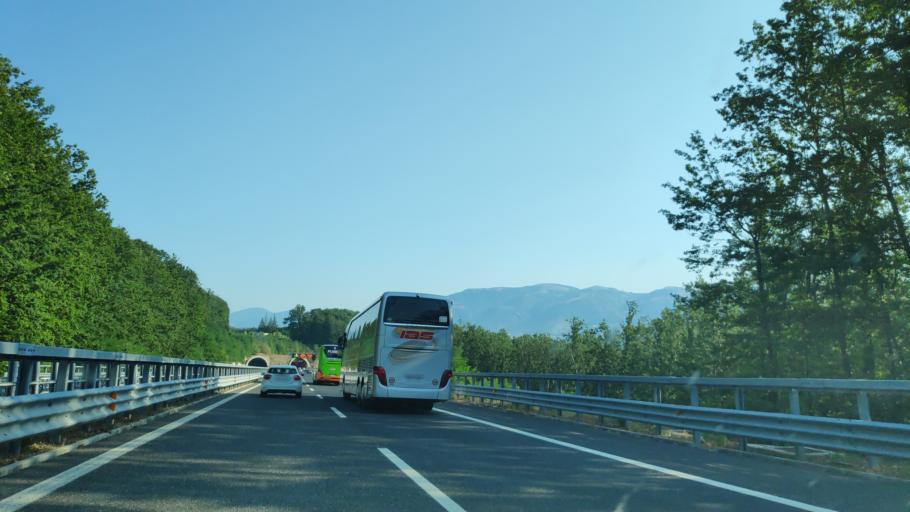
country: IT
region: Campania
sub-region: Provincia di Salerno
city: Casalbuono
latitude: 40.2483
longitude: 15.6601
